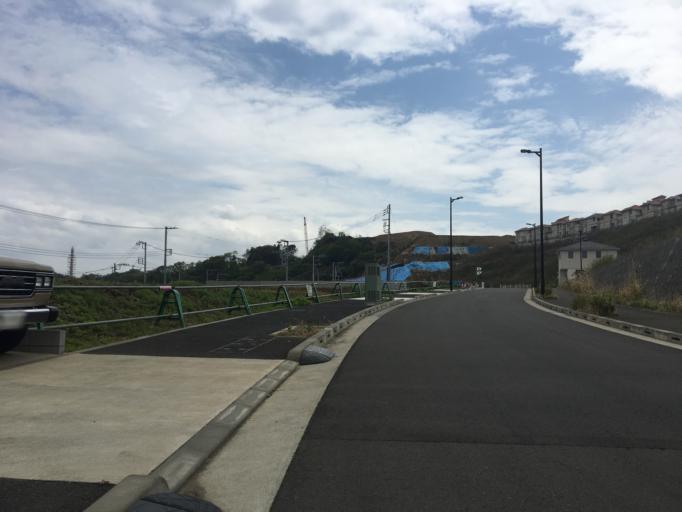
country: JP
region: Tokyo
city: Chofugaoka
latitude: 35.6334
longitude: 139.5066
